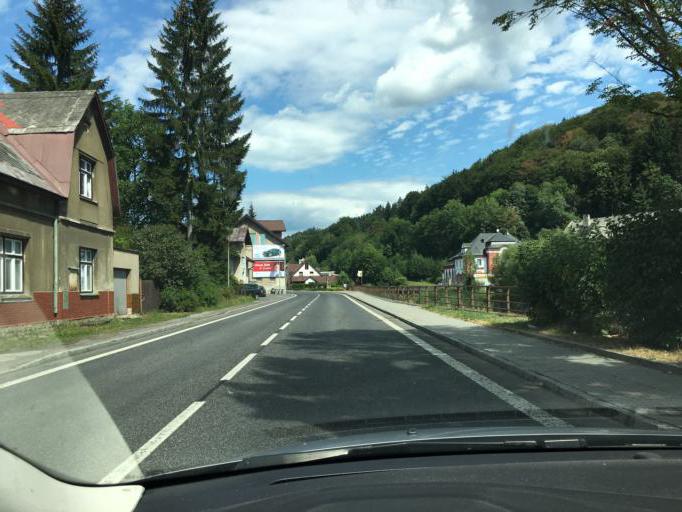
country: CZ
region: Liberecky
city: Velke Hamry
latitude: 50.7216
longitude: 15.3155
